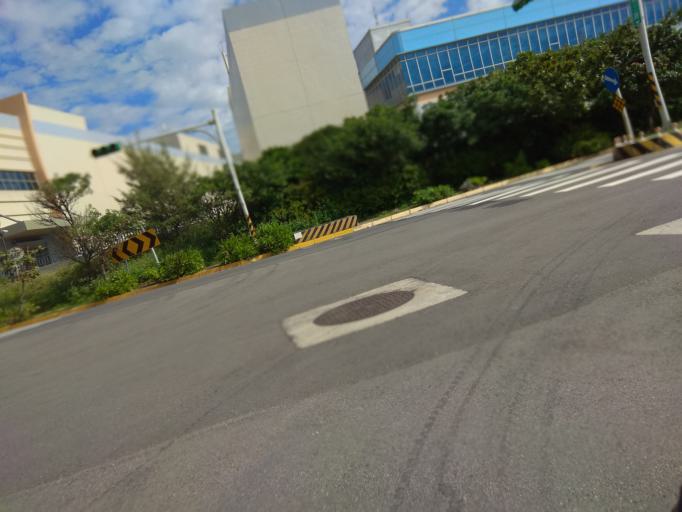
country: TW
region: Taiwan
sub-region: Hsinchu
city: Zhubei
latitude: 25.0380
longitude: 121.0700
